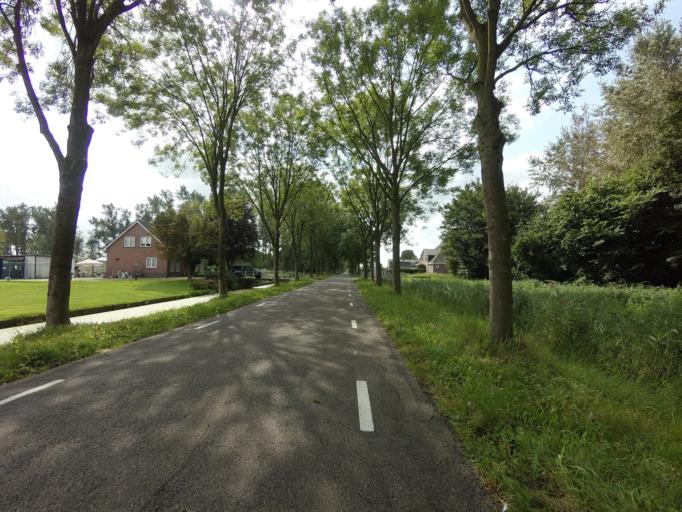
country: NL
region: North Holland
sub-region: Gemeente Purmerend
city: Purmerend
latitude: 52.4768
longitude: 4.9642
